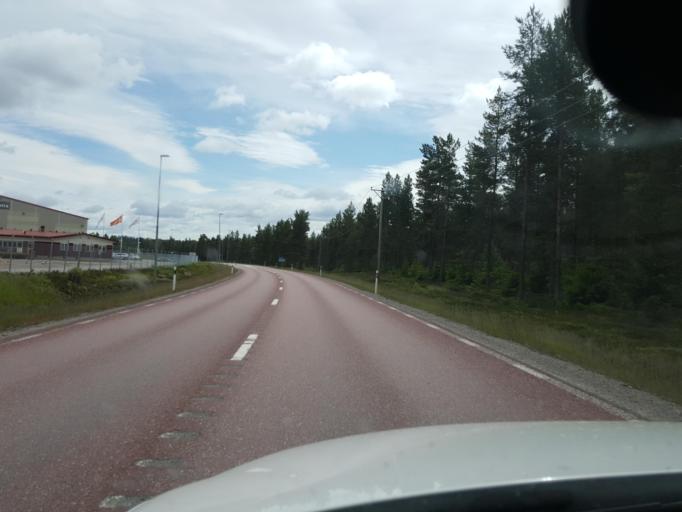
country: SE
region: Gaevleborg
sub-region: Ljusdals Kommun
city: Farila
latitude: 61.8053
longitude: 15.7799
